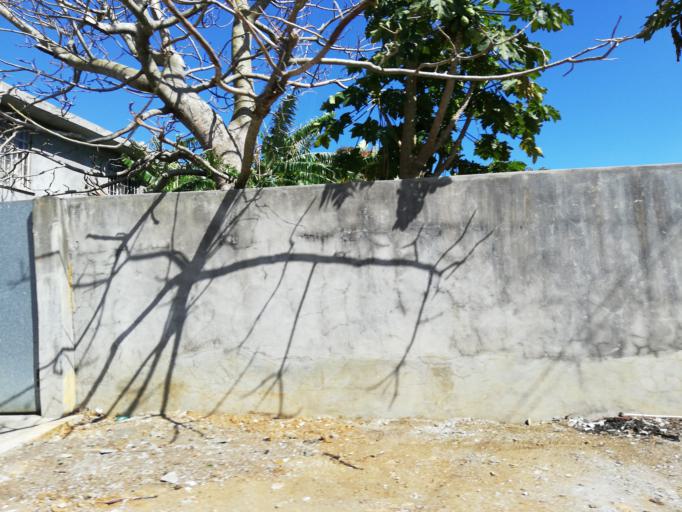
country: MU
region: Moka
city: Moka
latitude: -20.2309
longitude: 57.4996
